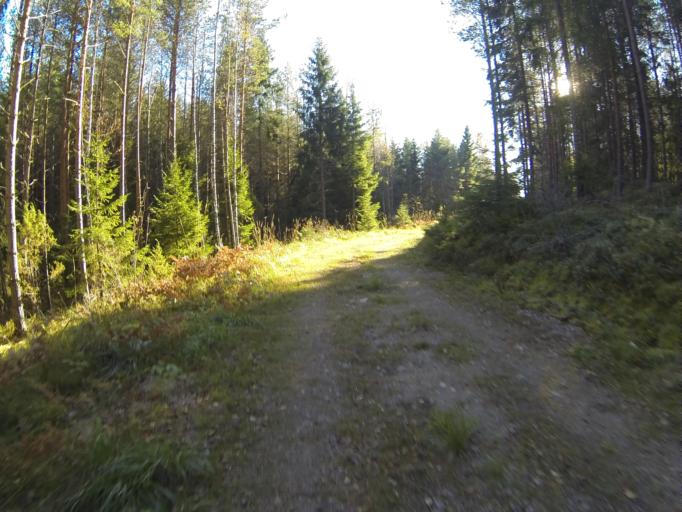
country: FI
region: Varsinais-Suomi
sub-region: Salo
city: Saerkisalo
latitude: 60.2232
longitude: 22.9438
